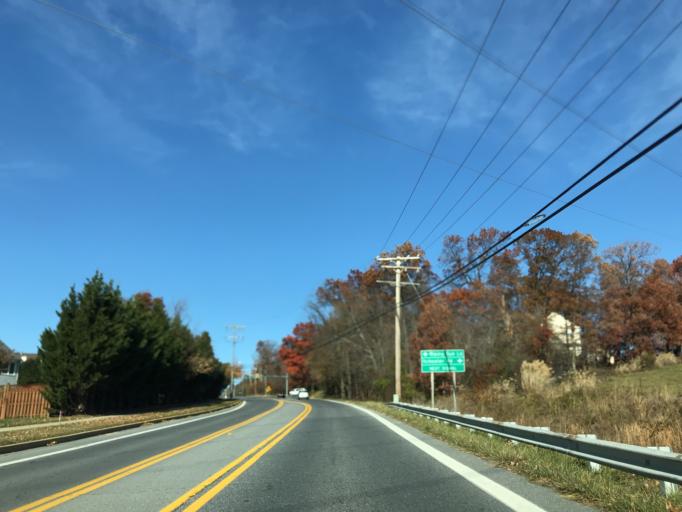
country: US
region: Maryland
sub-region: Howard County
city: Ilchester
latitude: 39.2255
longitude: -76.7897
